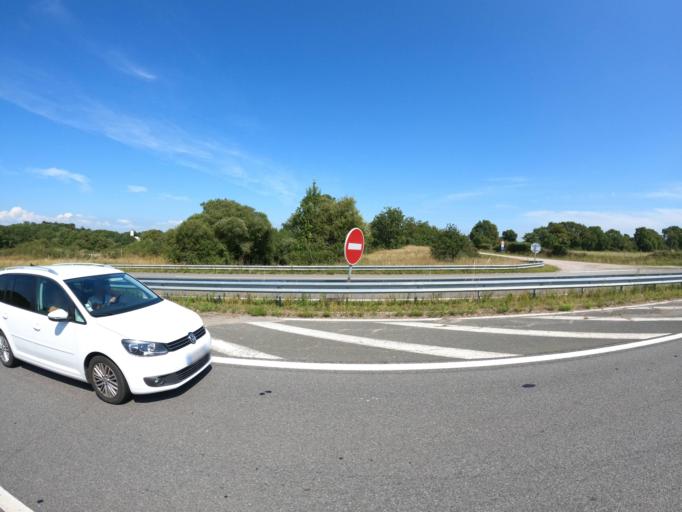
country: FR
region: Pays de la Loire
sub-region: Departement de la Loire-Atlantique
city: Saint-Michel-Chef-Chef
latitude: 47.1645
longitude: -2.1436
